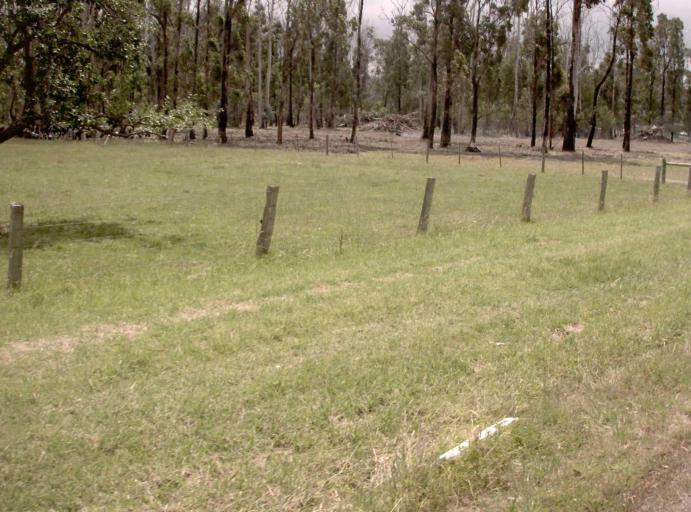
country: AU
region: Victoria
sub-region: Latrobe
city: Traralgon
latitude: -38.5332
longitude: 146.6582
